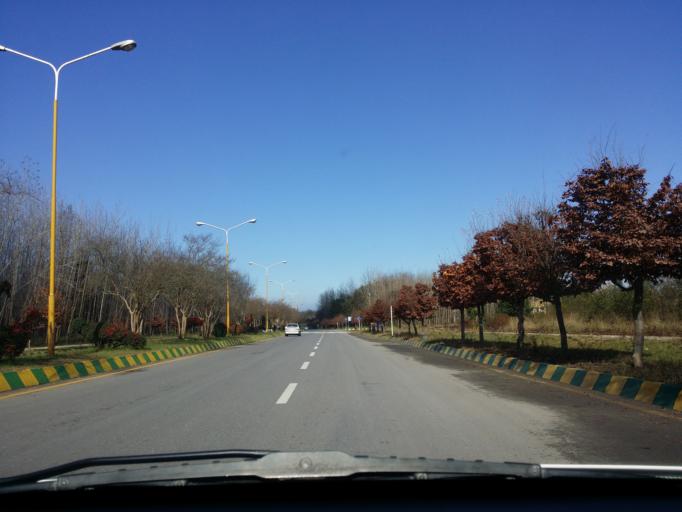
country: IR
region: Mazandaran
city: Chalus
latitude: 36.6770
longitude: 51.3067
